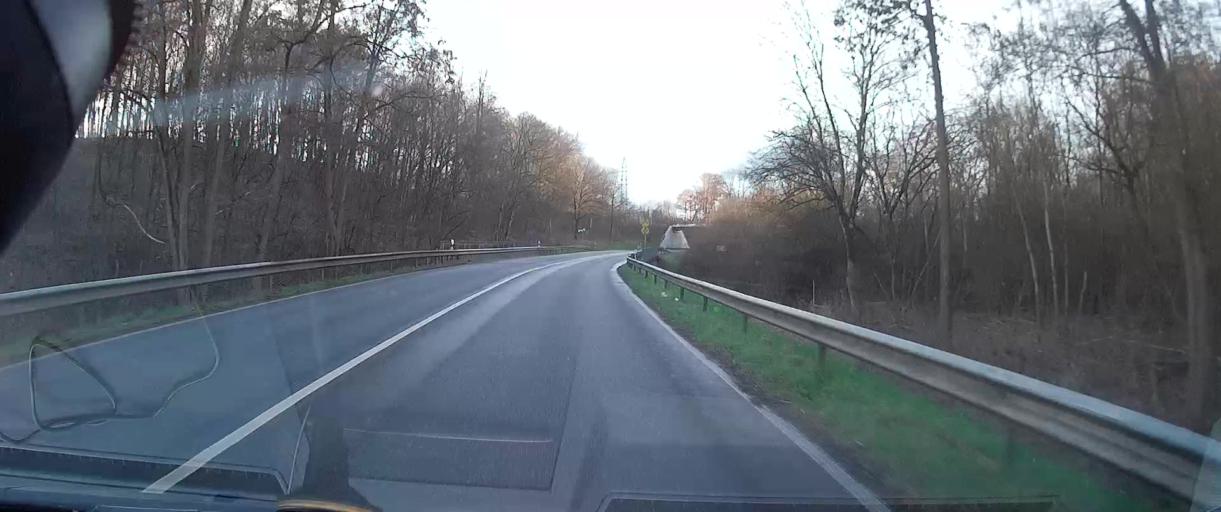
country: DE
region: Rheinland-Pfalz
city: Montabaur
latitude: 50.4519
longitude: 7.8113
